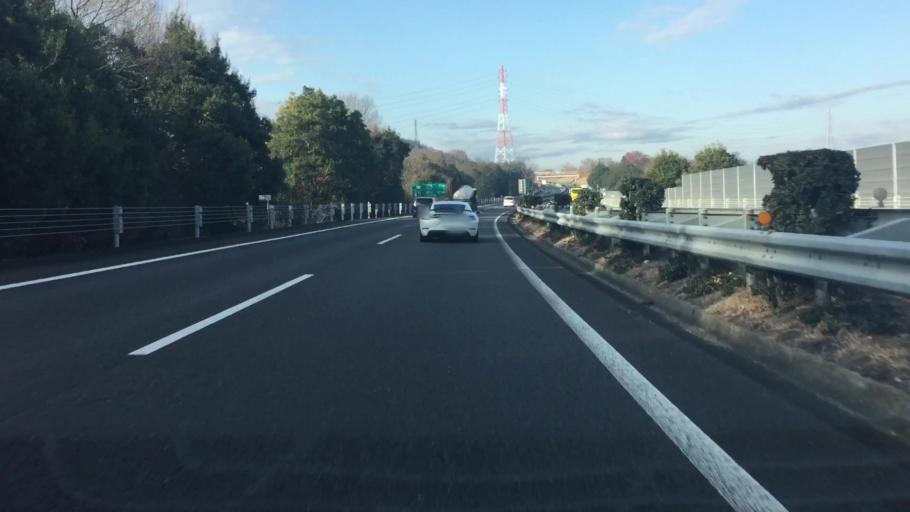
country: JP
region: Gunma
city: Yoshii
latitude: 36.2409
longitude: 138.9822
